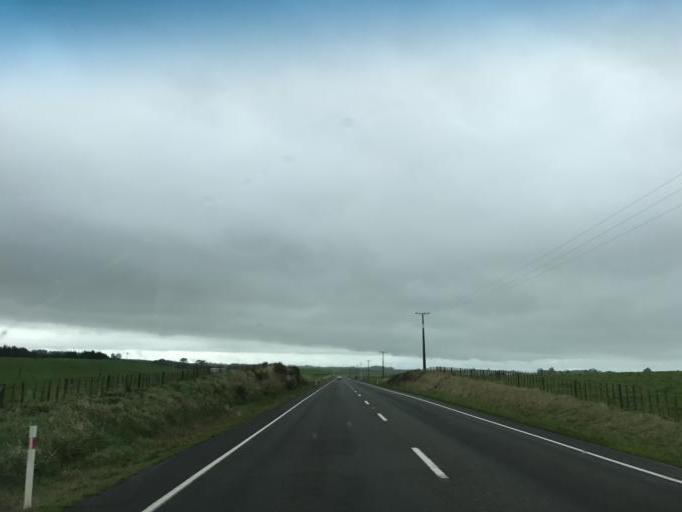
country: NZ
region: Manawatu-Wanganui
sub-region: Wanganui District
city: Wanganui
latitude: -39.8147
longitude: 174.8161
